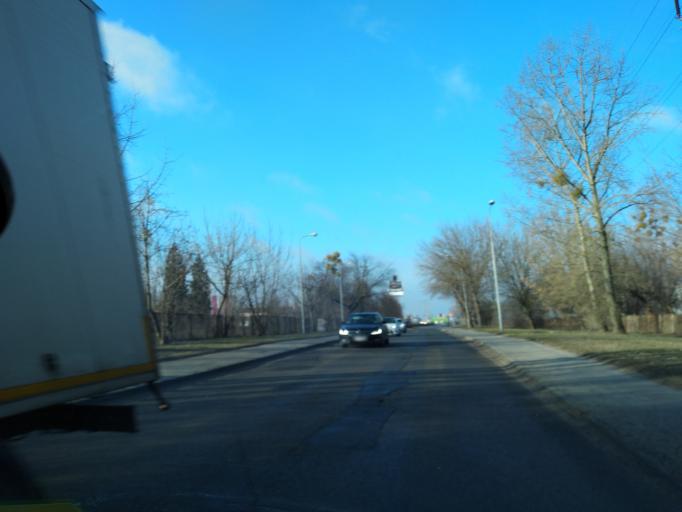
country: PL
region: Masovian Voivodeship
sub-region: Powiat piaseczynski
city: Piaseczno
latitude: 52.0894
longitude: 21.0250
